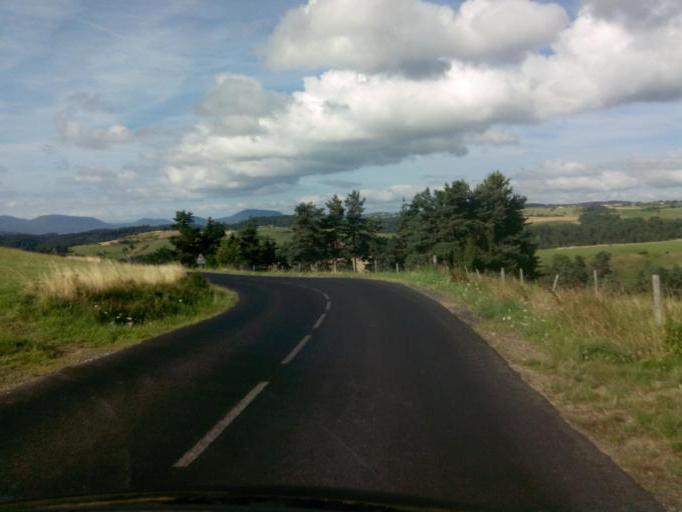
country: FR
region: Auvergne
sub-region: Departement de la Haute-Loire
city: Bas-en-Basset
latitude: 45.3196
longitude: 4.0773
